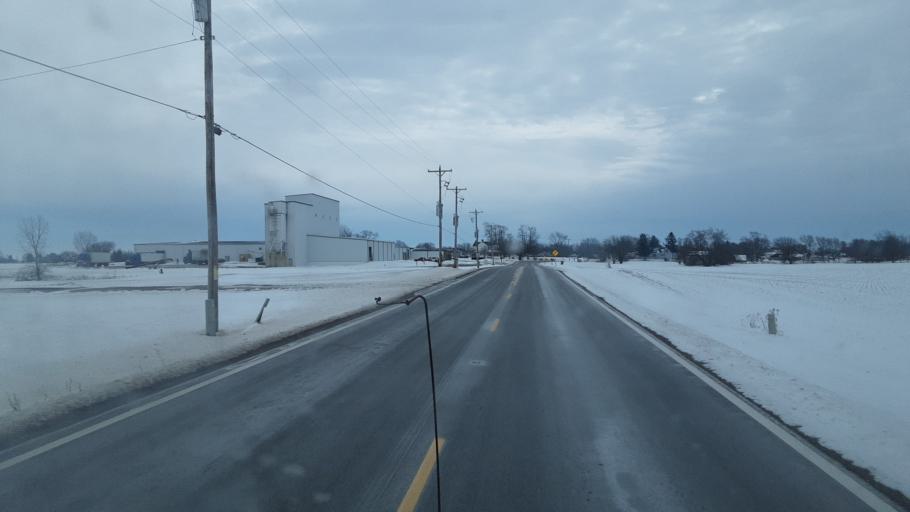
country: US
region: Ohio
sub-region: Madison County
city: Bethel
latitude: 39.7402
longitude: -83.4782
